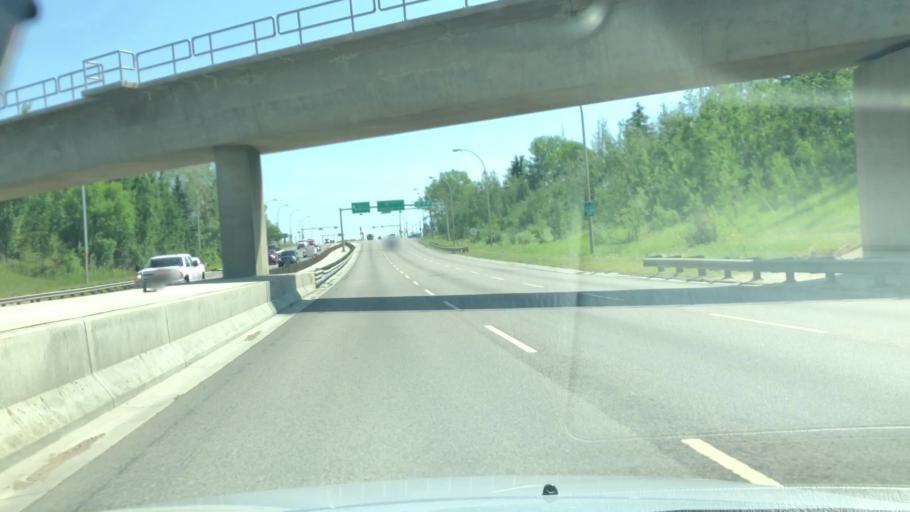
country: CA
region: Alberta
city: Edmonton
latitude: 53.5806
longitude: -113.5308
